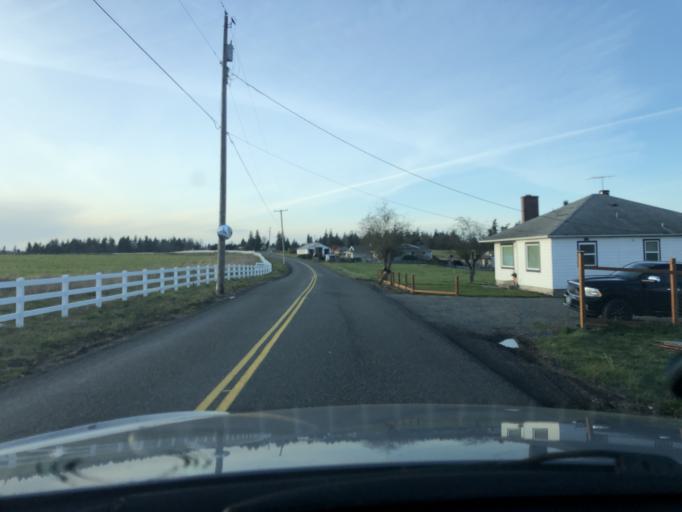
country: US
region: Washington
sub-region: Pierce County
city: Prairie Ridge
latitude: 47.1973
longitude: -122.1147
